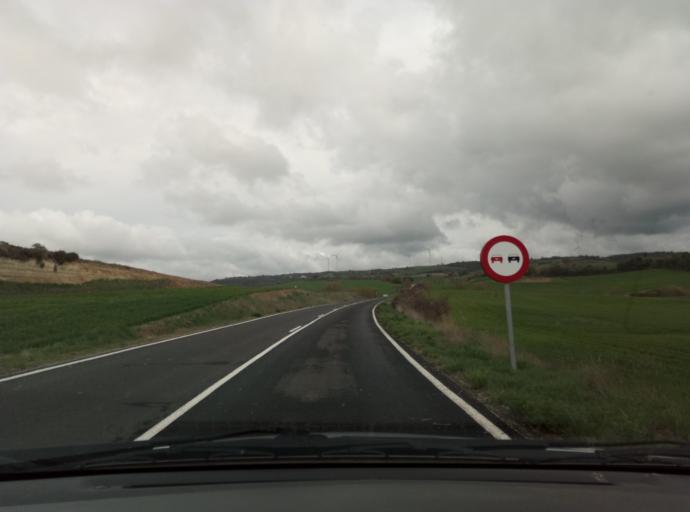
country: ES
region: Catalonia
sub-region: Provincia de Tarragona
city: Santa Coloma de Queralt
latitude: 41.5703
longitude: 1.3471
